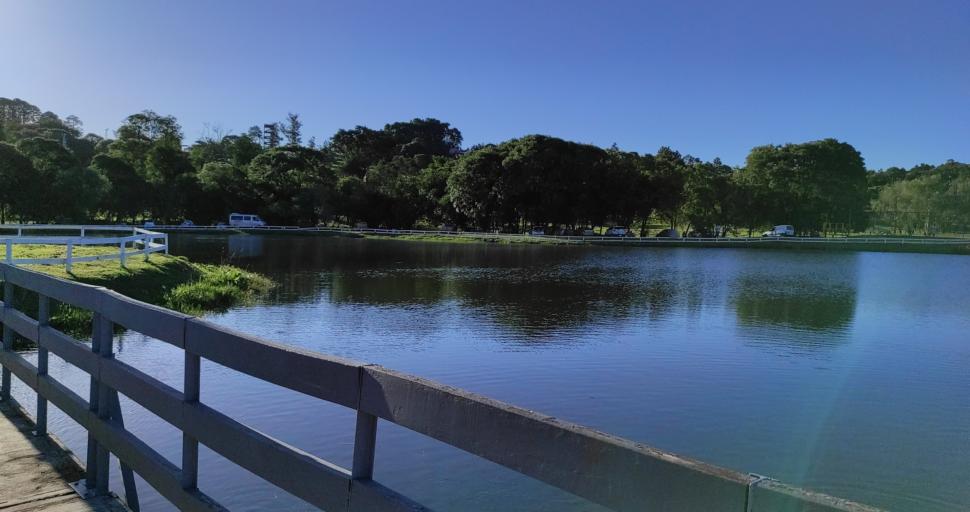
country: AR
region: Misiones
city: Dos de Mayo
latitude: -27.0418
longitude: -54.6799
